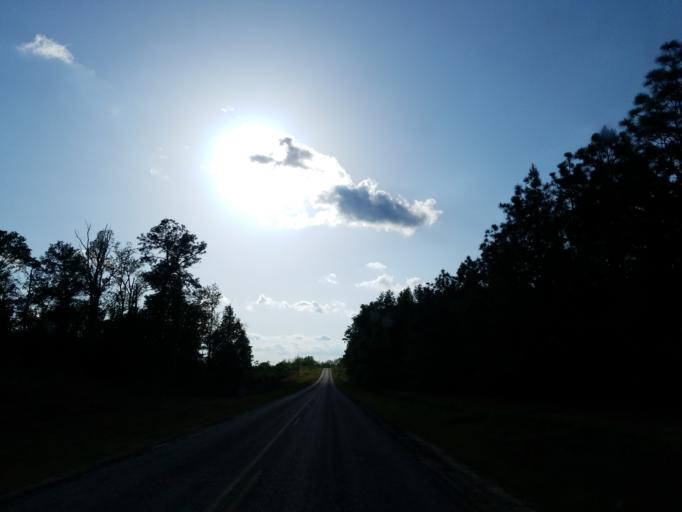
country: US
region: Georgia
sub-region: Turner County
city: Ashburn
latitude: 31.6085
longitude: -83.5913
